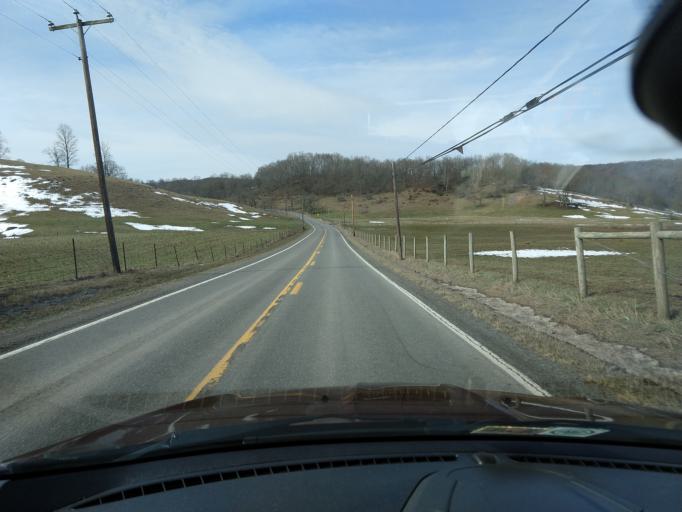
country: US
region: West Virginia
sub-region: Pocahontas County
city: Marlinton
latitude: 38.1266
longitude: -80.2319
